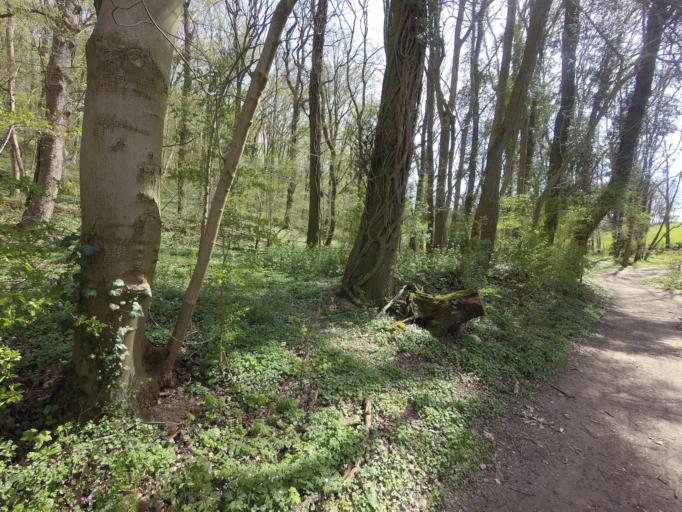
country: NL
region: Limburg
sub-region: Eijsden-Margraten
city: Eijsden
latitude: 50.7754
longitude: 5.7667
